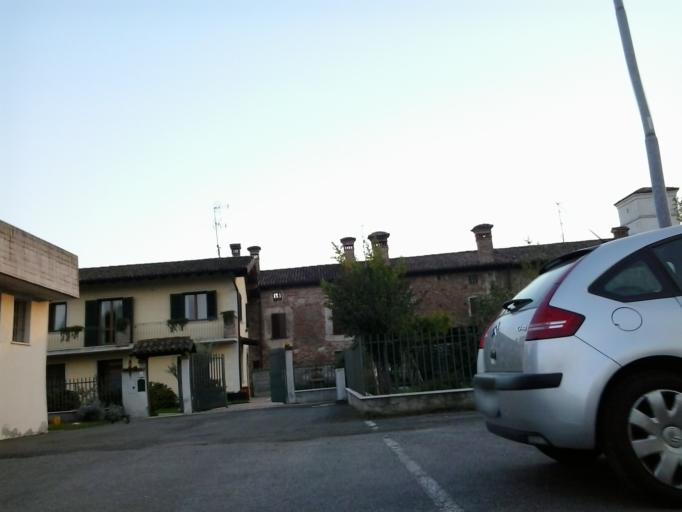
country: IT
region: Lombardy
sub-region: Provincia di Brescia
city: Azzano Mella
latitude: 45.4243
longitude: 10.1206
